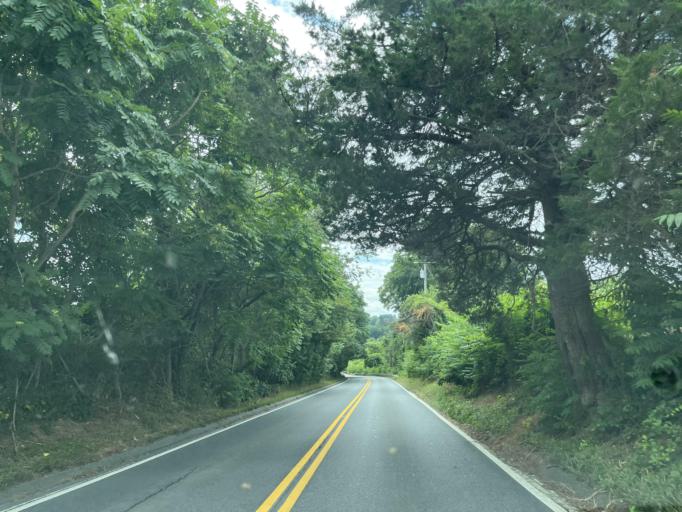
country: US
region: Maryland
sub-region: Montgomery County
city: Damascus
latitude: 39.2374
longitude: -77.1816
